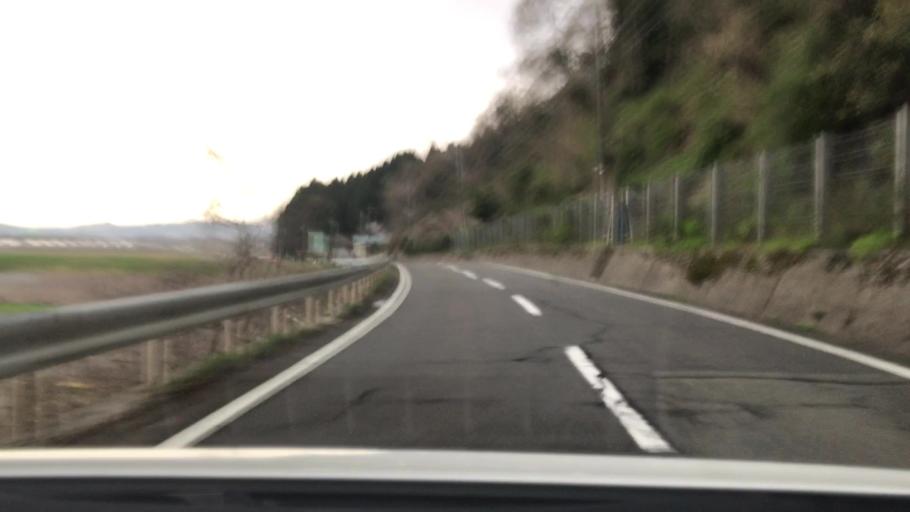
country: JP
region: Fukui
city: Fukui-shi
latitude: 36.0814
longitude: 136.1793
